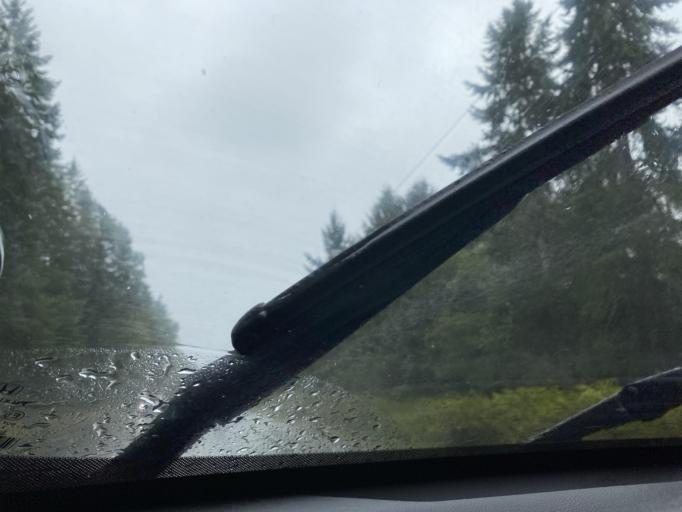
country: US
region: Washington
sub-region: Kitsap County
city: Suquamish
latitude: 47.6822
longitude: -122.5422
